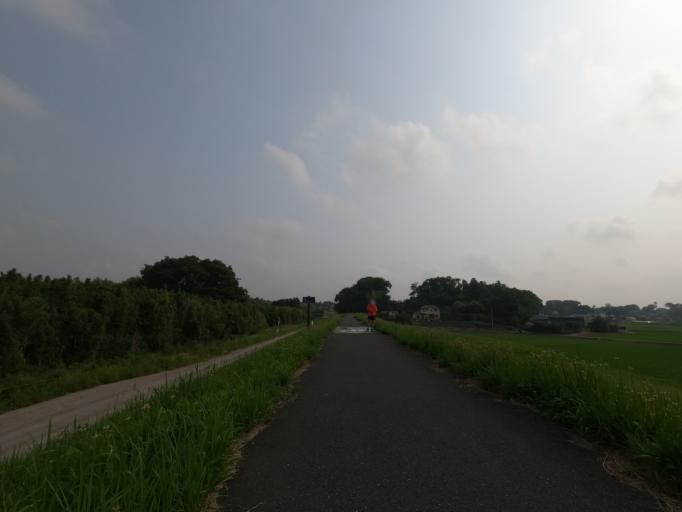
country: JP
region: Ibaraki
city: Moriya
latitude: 35.9579
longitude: 139.9486
